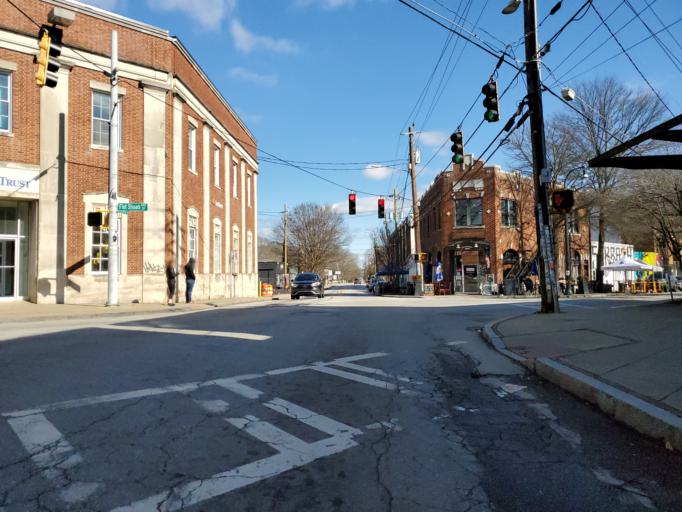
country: US
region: Georgia
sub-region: DeKalb County
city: Druid Hills
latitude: 33.7402
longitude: -84.3454
